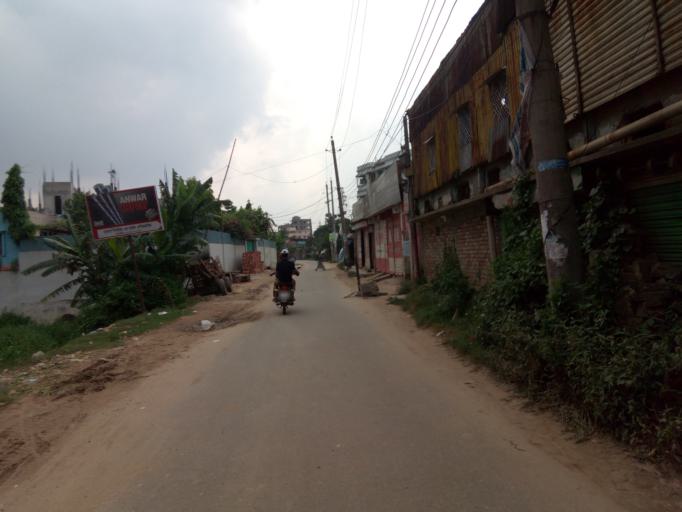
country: BD
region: Dhaka
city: Paltan
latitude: 23.7454
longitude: 90.4601
